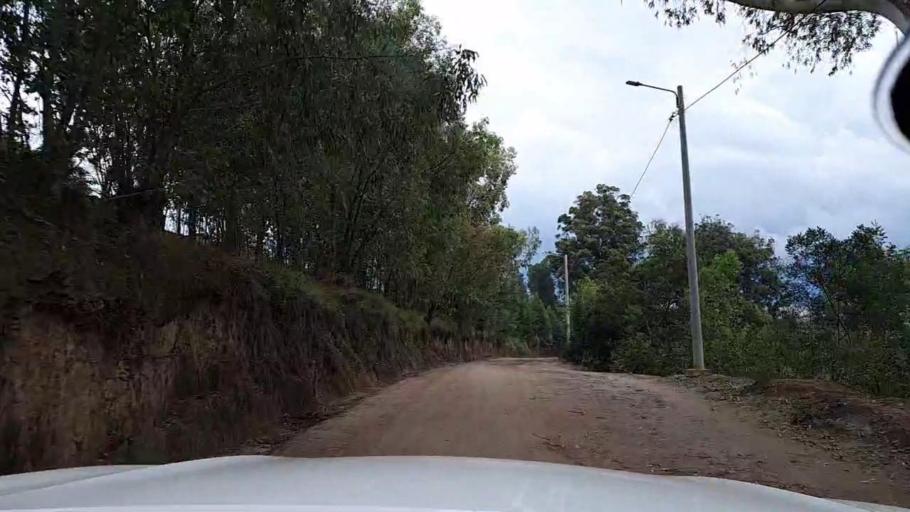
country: BI
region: Kayanza
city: Kayanza
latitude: -2.7984
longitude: 29.5065
